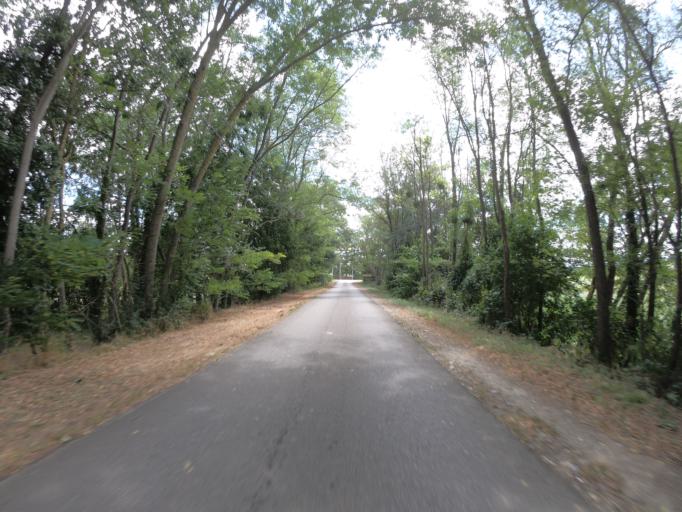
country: FR
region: Midi-Pyrenees
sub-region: Departement de l'Ariege
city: La Tour-du-Crieu
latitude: 43.0976
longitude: 1.7333
